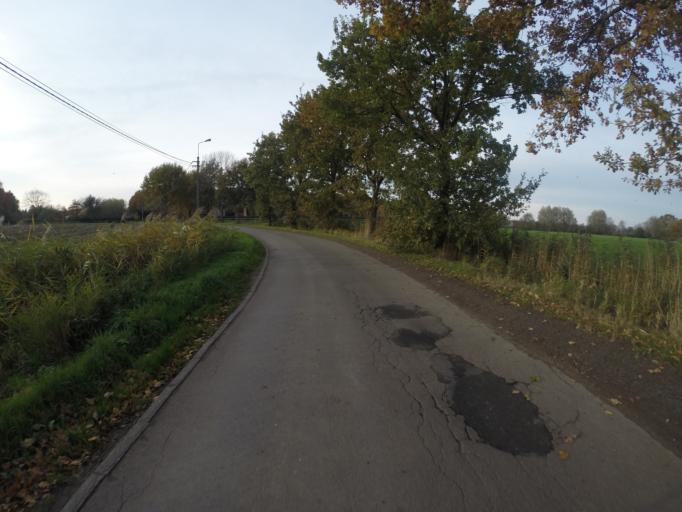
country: BE
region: Flanders
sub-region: Provincie Oost-Vlaanderen
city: Aalter
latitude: 51.0710
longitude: 3.4991
